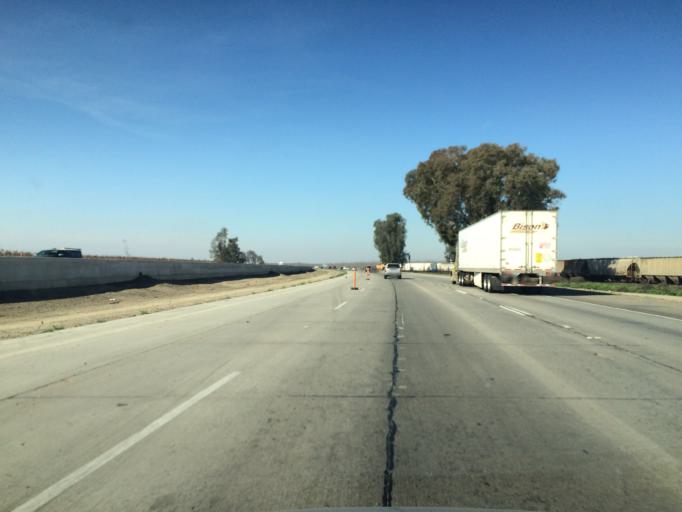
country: US
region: California
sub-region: Tulare County
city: Goshen
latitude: 36.3608
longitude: -119.4287
